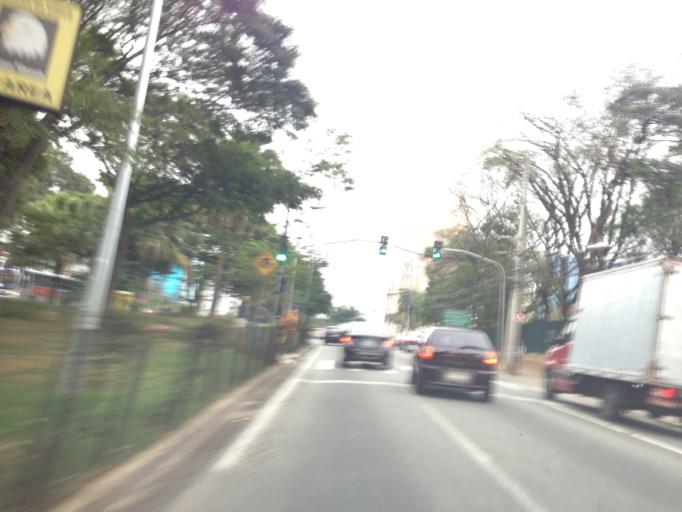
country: BR
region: Sao Paulo
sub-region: Carapicuiba
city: Carapicuiba
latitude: -23.5004
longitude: -46.8480
